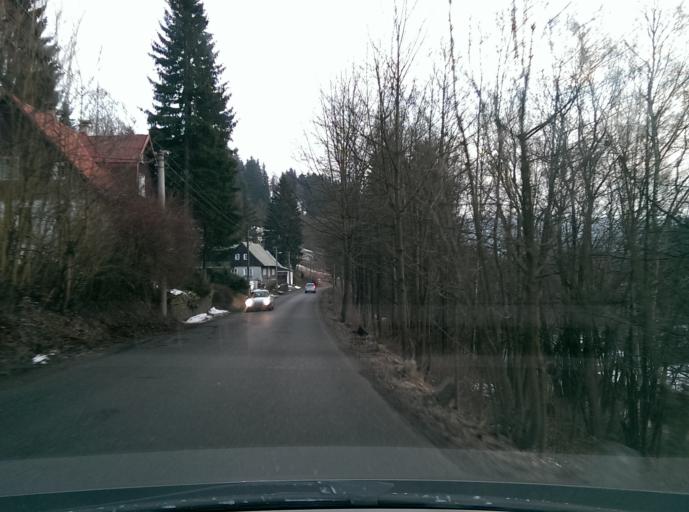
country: CZ
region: Liberecky
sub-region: Okres Jablonec nad Nisou
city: Smrzovka
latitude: 50.7517
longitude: 15.2663
